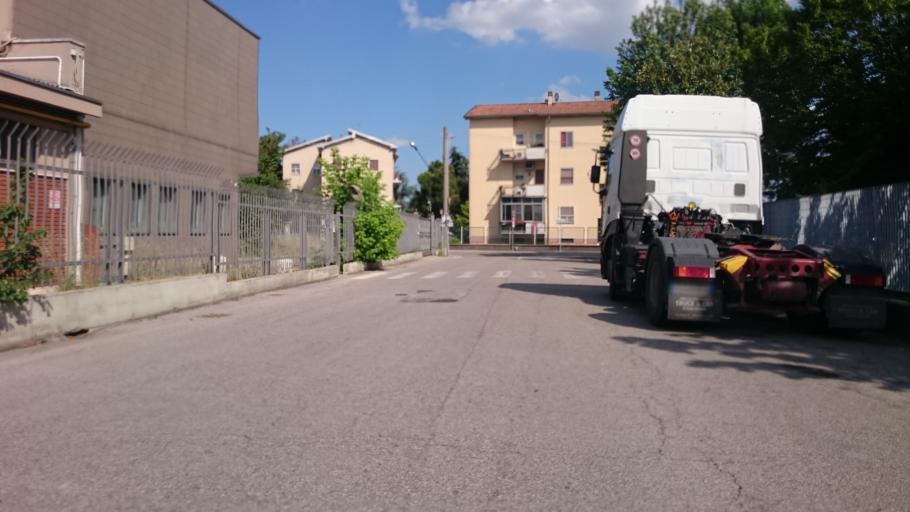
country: IT
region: Lombardy
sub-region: Provincia di Mantova
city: Lunetta-Frassino
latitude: 45.1526
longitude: 10.8329
